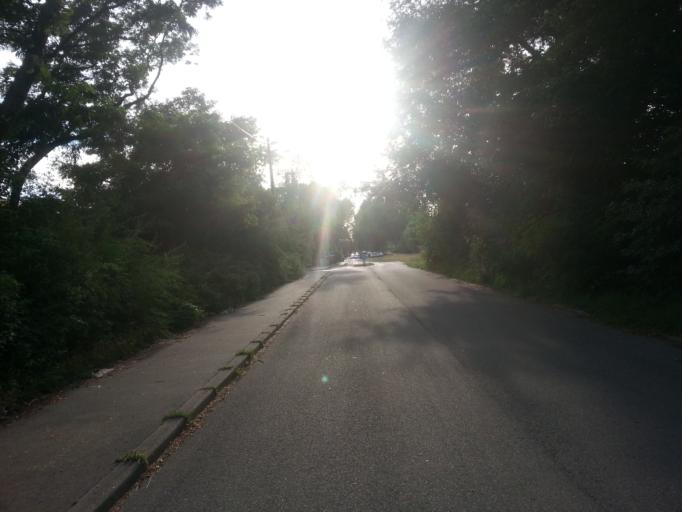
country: DE
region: Rheinland-Pfalz
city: Altrip
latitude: 49.4477
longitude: 8.4907
